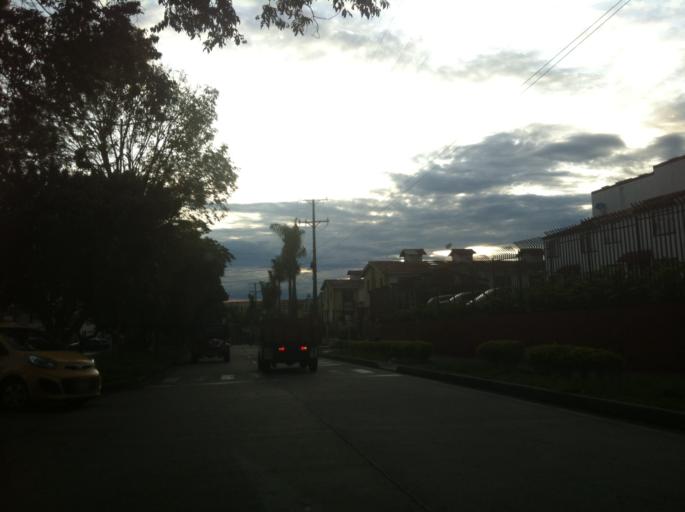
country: CO
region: Quindio
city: Calarca
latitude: 4.5645
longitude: -75.6554
